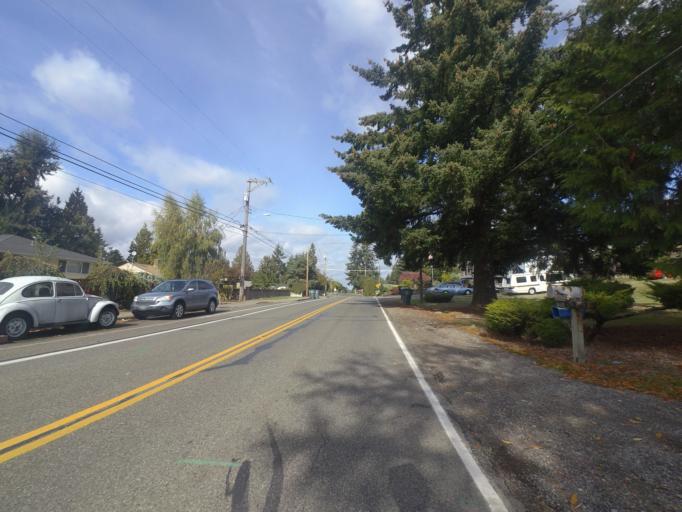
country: US
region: Washington
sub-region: Pierce County
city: University Place
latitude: 47.2268
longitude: -122.5450
